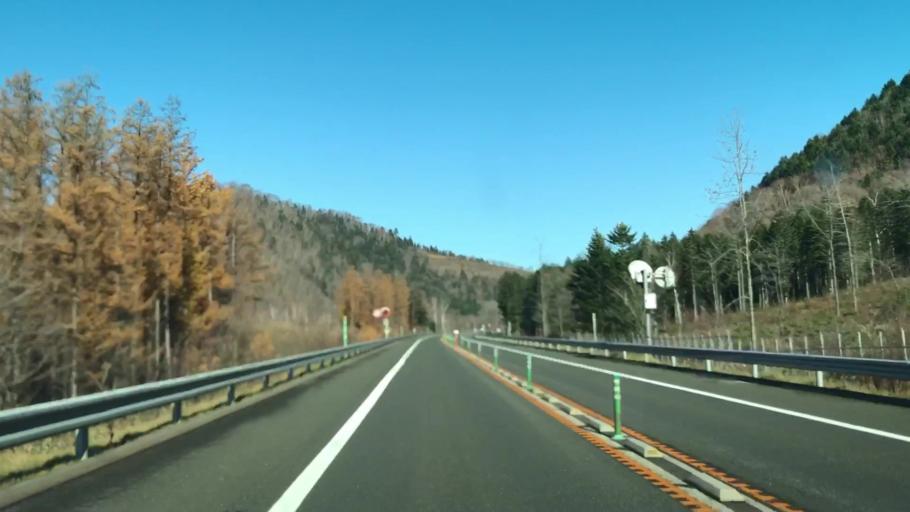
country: JP
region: Hokkaido
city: Shimo-furano
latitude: 43.0176
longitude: 142.4347
